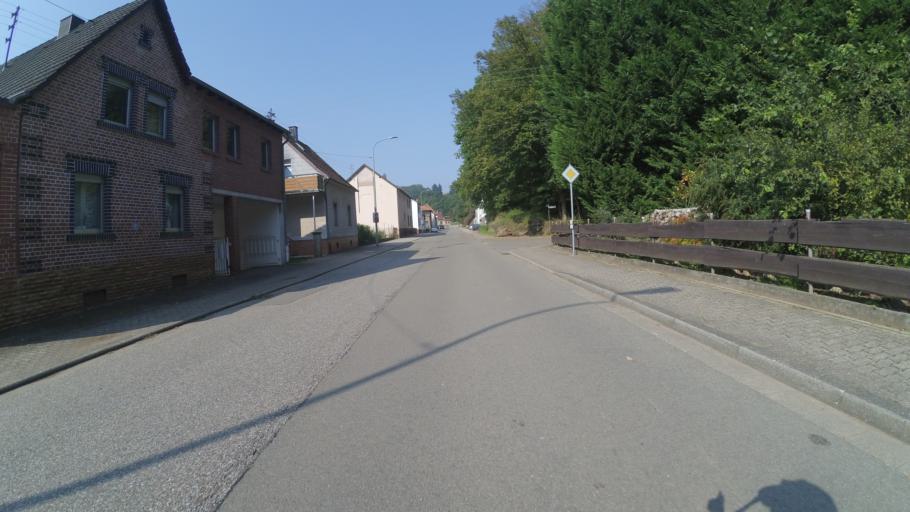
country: DE
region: Rheinland-Pfalz
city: Rieschweiler-Muhlbach
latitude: 49.2491
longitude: 7.5127
